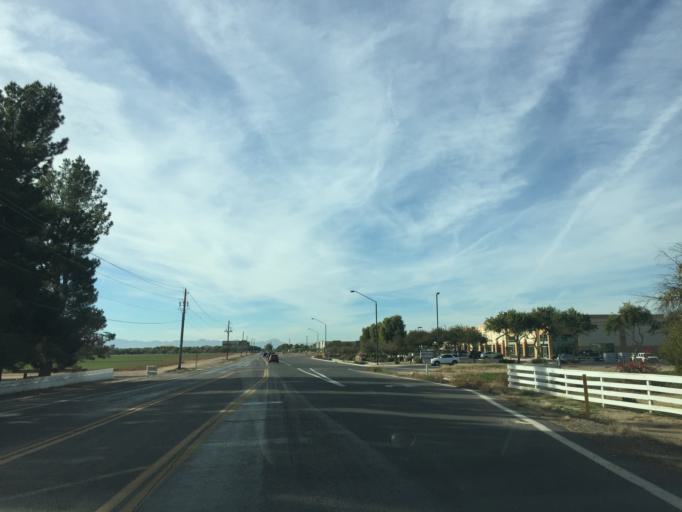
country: US
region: Arizona
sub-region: Maricopa County
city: Chandler
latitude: 33.2776
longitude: -111.7757
